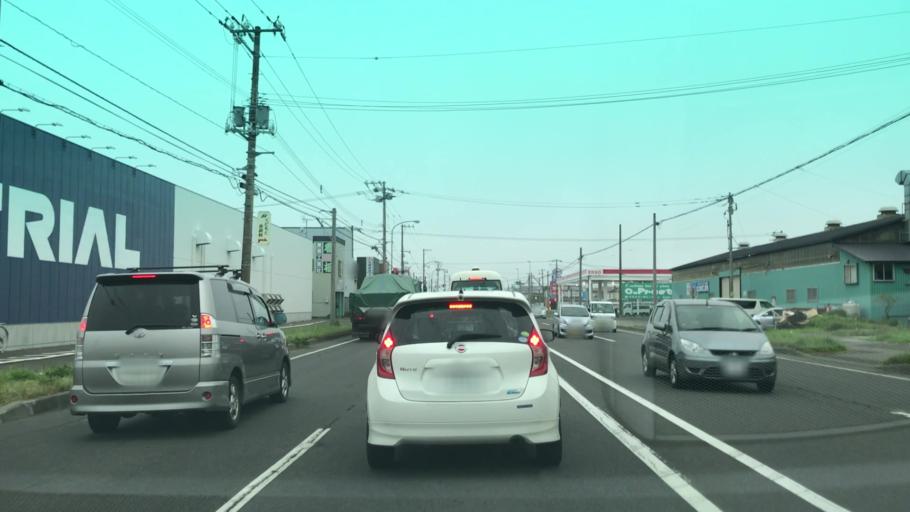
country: JP
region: Hokkaido
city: Muroran
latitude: 42.3798
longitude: 141.0724
